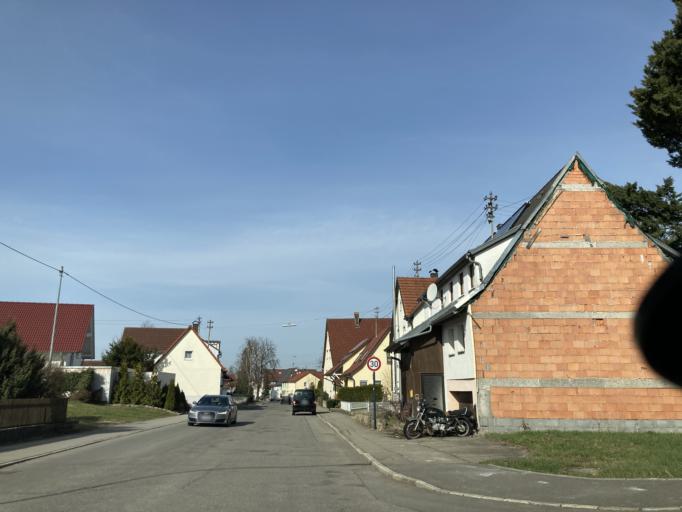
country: DE
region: Baden-Wuerttemberg
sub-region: Tuebingen Region
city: Mossingen
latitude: 48.4049
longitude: 9.0643
